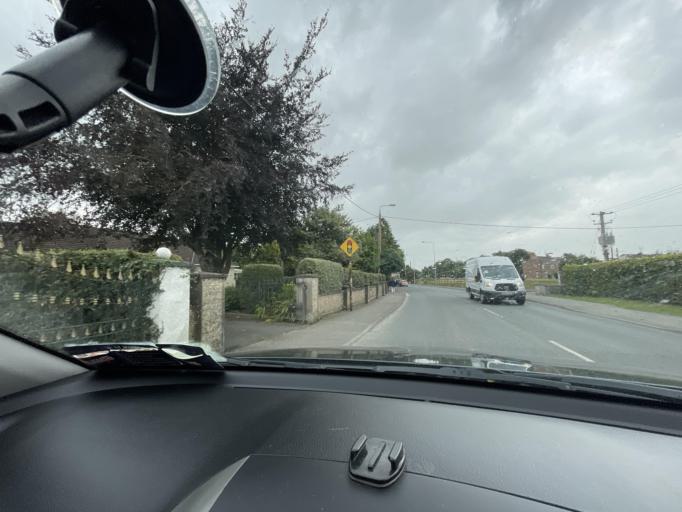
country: IE
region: Leinster
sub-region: Lu
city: Drogheda
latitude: 53.7247
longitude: -6.3621
